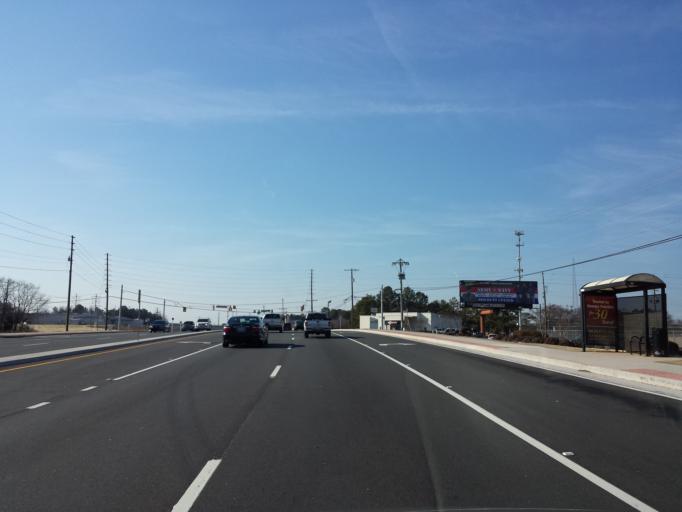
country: US
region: Georgia
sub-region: Cobb County
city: Marietta
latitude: 33.9745
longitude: -84.5437
